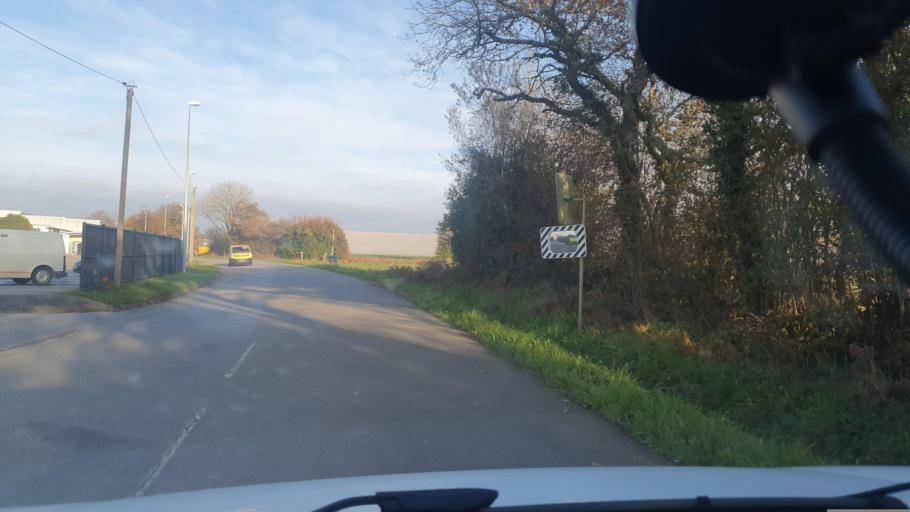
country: FR
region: Brittany
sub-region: Departement du Finistere
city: Briec
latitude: 48.0954
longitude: -4.0228
